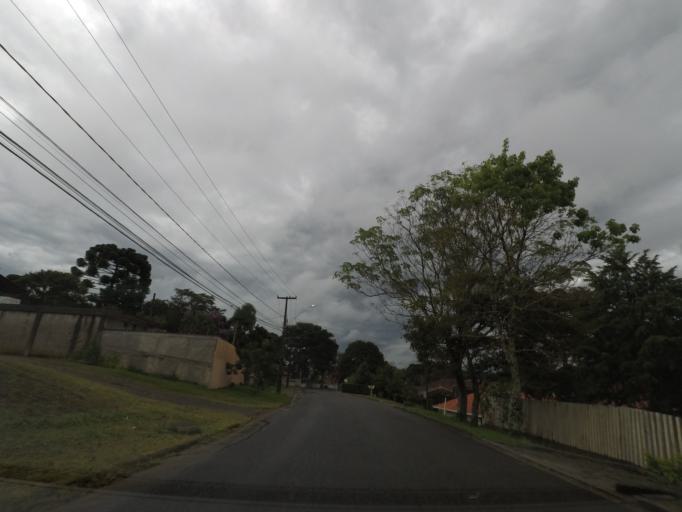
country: BR
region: Parana
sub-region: Campo Largo
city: Campo Largo
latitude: -25.4498
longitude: -49.4546
